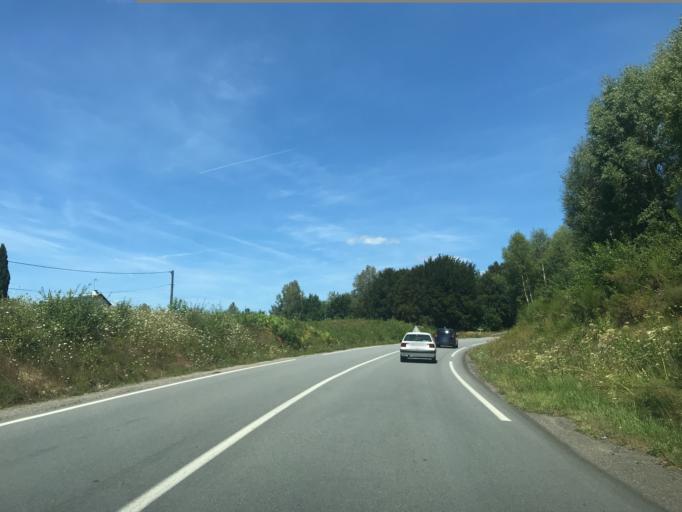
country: FR
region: Limousin
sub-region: Departement de la Correze
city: Egletons
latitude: 45.3935
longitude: 2.0315
